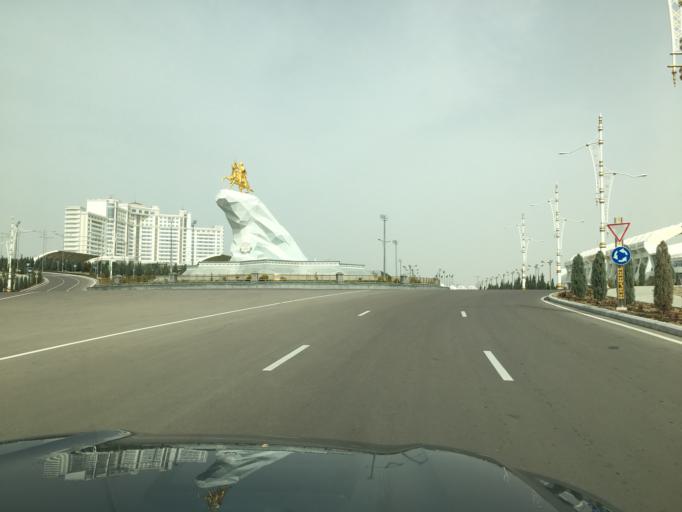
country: TM
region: Ahal
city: Ashgabat
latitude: 37.9247
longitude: 58.3494
